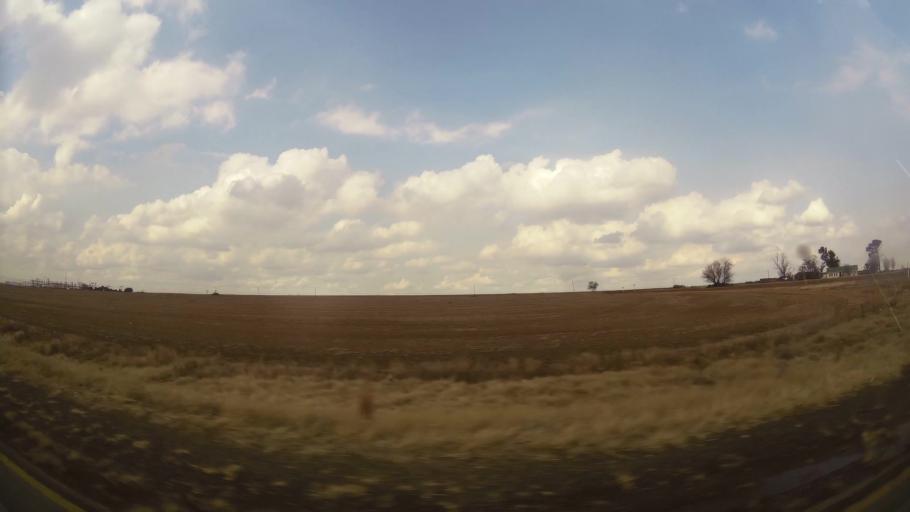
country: ZA
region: Orange Free State
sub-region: Fezile Dabi District Municipality
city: Sasolburg
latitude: -26.8275
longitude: 27.9007
